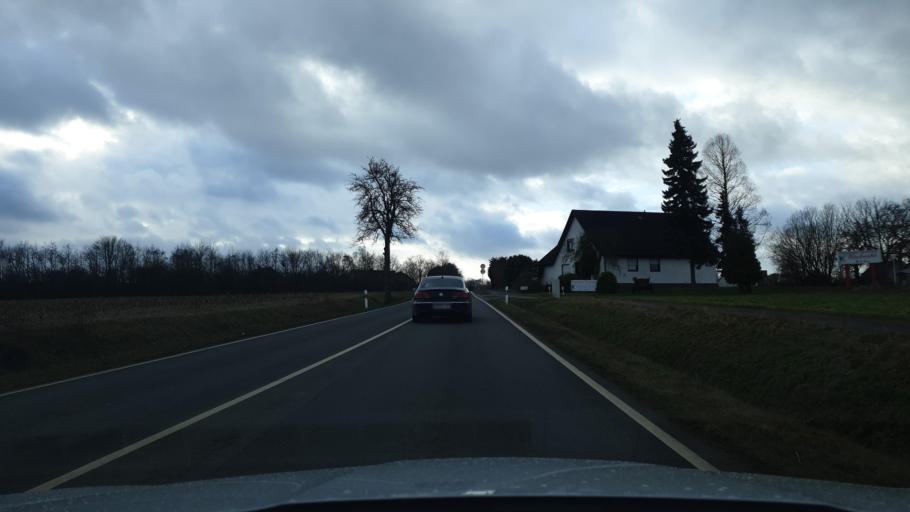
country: DE
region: North Rhine-Westphalia
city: Bad Oeynhausen
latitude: 52.1736
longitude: 8.8037
